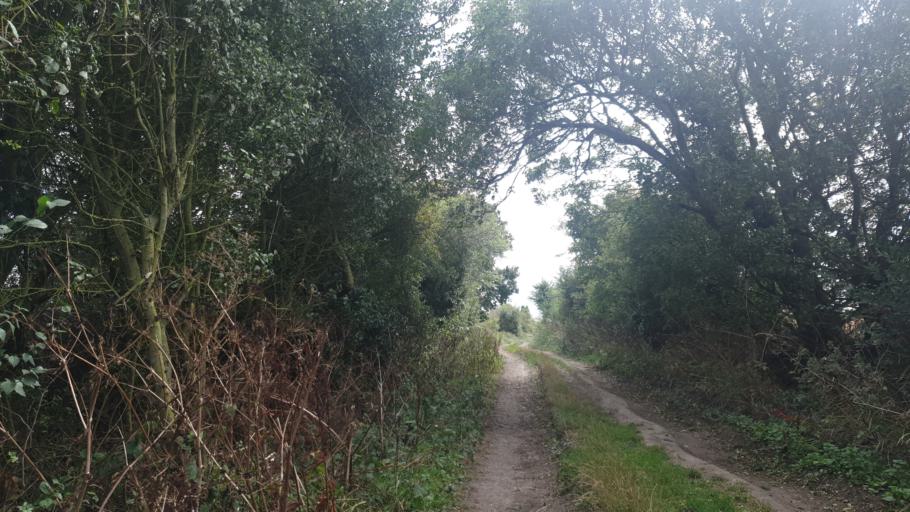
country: GB
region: England
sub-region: Essex
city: Frinton-on-Sea
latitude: 51.8491
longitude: 1.2363
